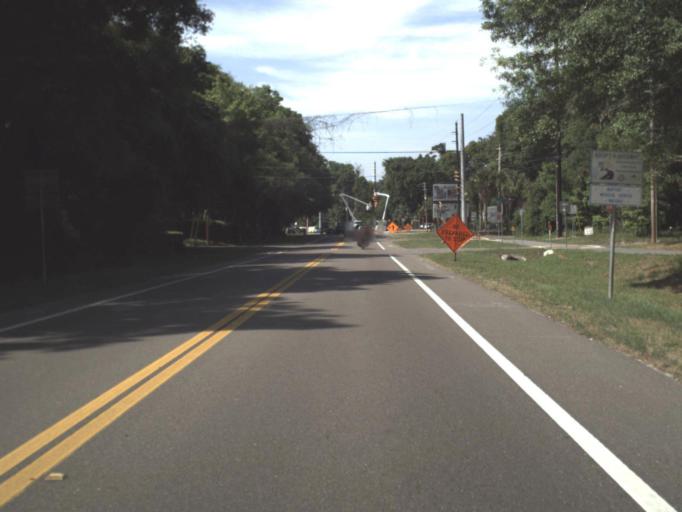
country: US
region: Florida
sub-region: Nassau County
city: Fernandina Beach
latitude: 30.5776
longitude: -81.4539
